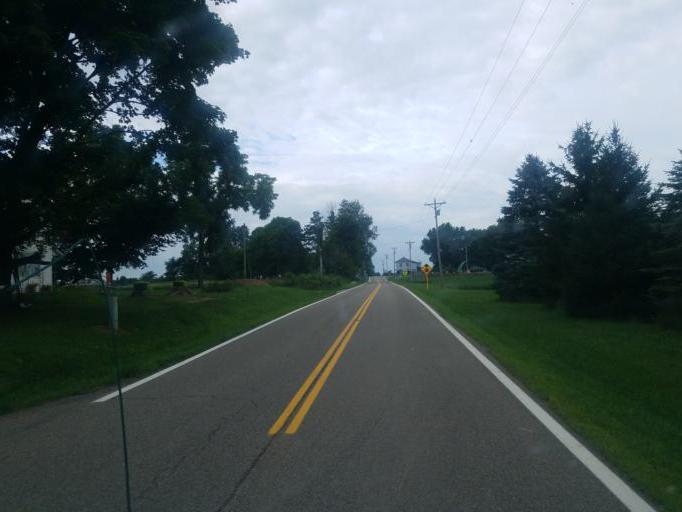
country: US
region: Ohio
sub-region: Knox County
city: Oak Hill
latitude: 40.4163
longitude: -82.1381
